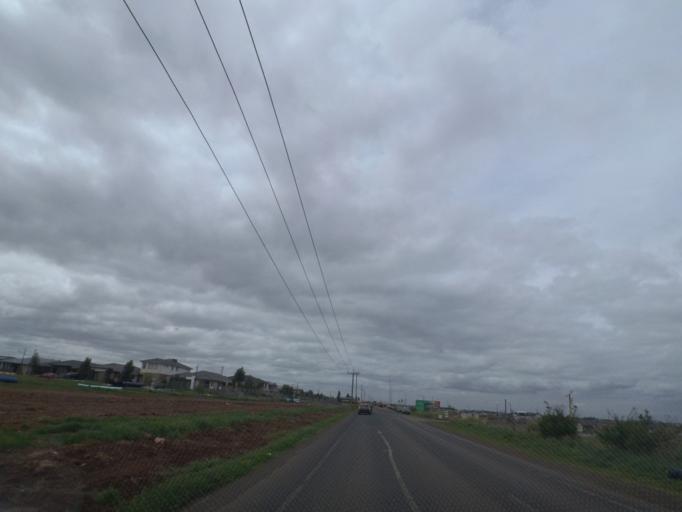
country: AU
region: Victoria
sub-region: Melton
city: Caroline Springs
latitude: -37.7198
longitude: 144.7199
